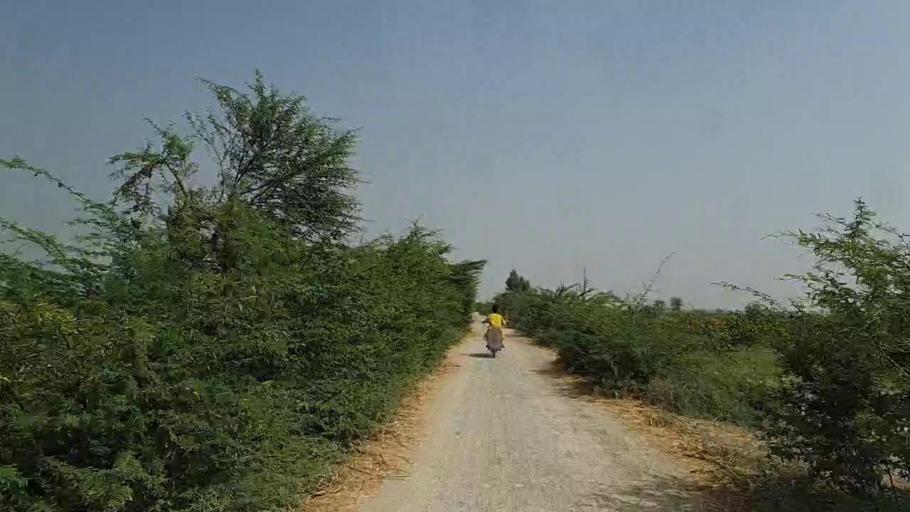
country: PK
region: Sindh
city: Naukot
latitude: 24.7778
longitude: 69.3546
